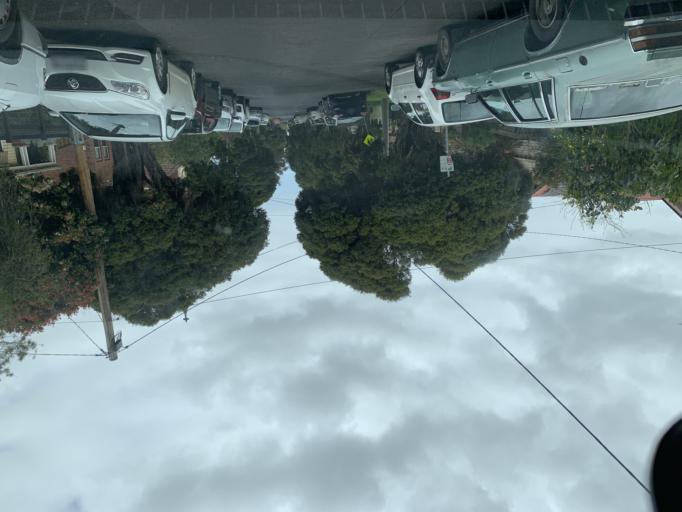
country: AU
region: Victoria
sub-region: Moreland
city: Pascoe Vale South
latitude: -37.7491
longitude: 144.9531
